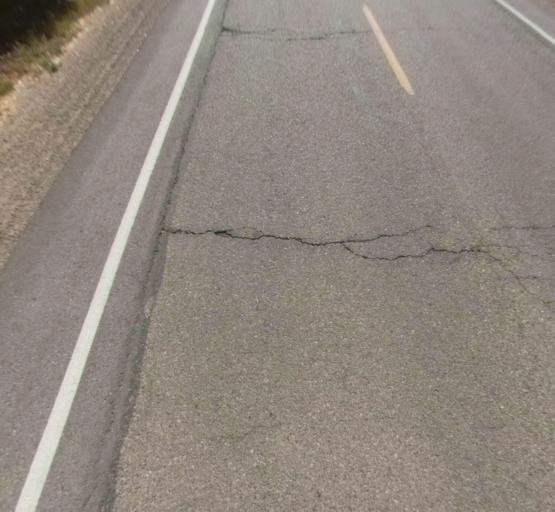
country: US
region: California
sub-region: Madera County
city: Chowchilla
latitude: 37.1127
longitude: -120.3711
